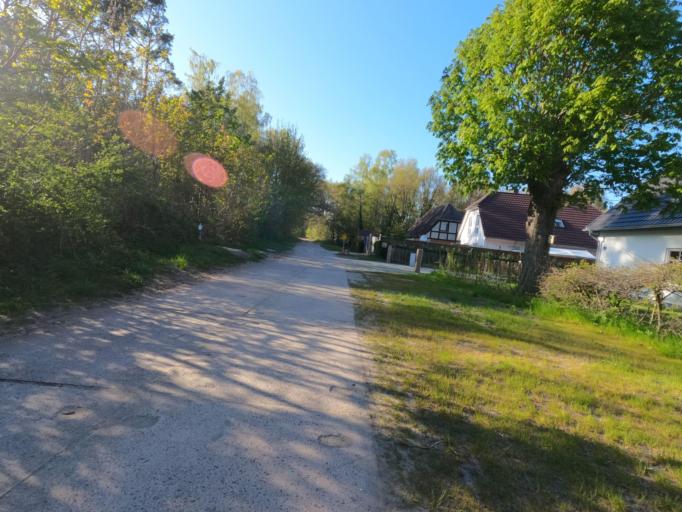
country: DE
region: Mecklenburg-Vorpommern
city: Born
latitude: 54.3916
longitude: 12.5372
